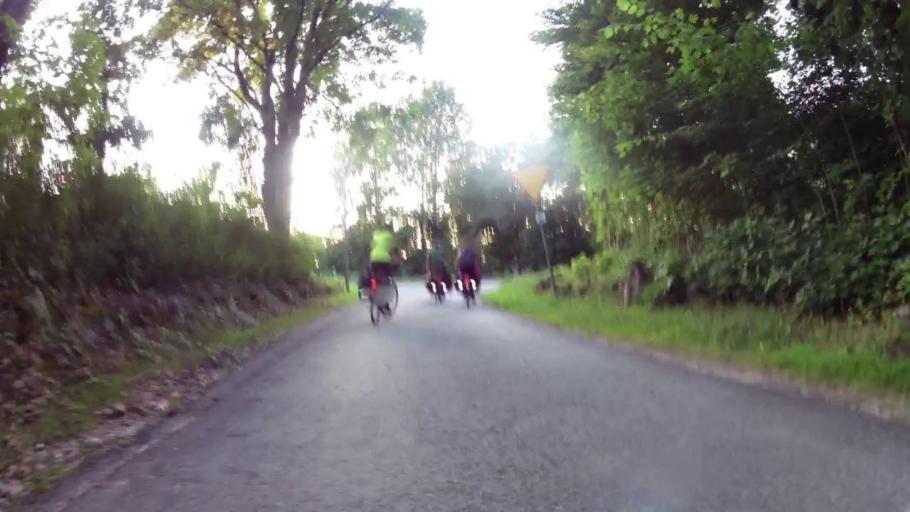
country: PL
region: West Pomeranian Voivodeship
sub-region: Powiat drawski
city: Drawsko Pomorskie
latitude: 53.4987
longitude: 15.7414
